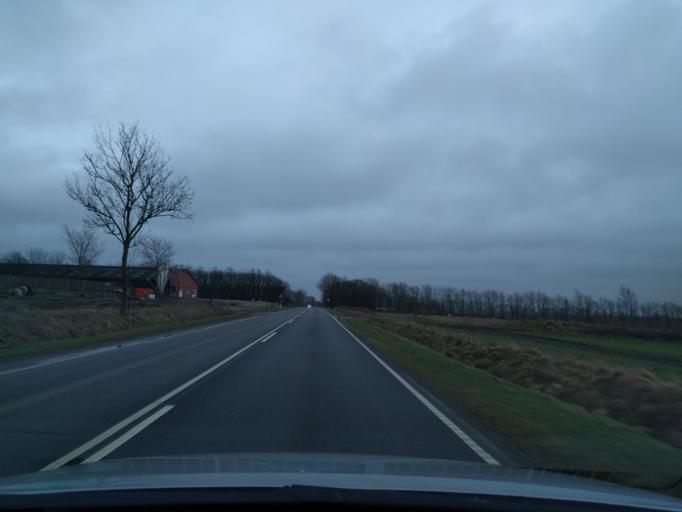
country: DK
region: South Denmark
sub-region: Haderslev Kommune
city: Vojens
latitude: 55.2435
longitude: 9.2111
